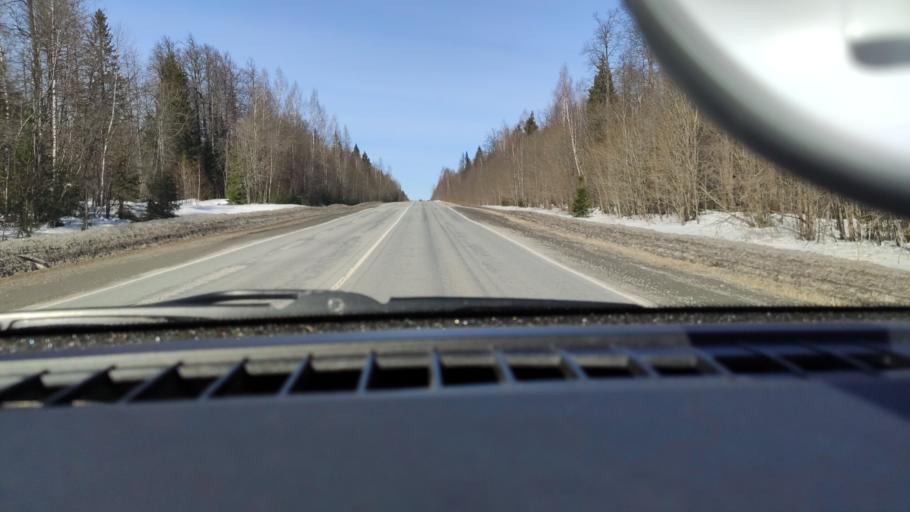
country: RU
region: Perm
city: Perm
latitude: 58.1748
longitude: 56.2308
